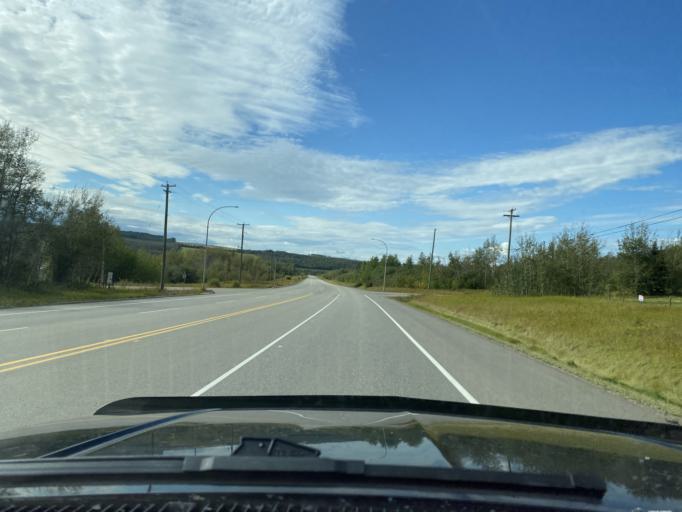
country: CA
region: British Columbia
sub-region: Peace River Regional District
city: Dawson Creek
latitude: 55.8839
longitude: -120.4522
